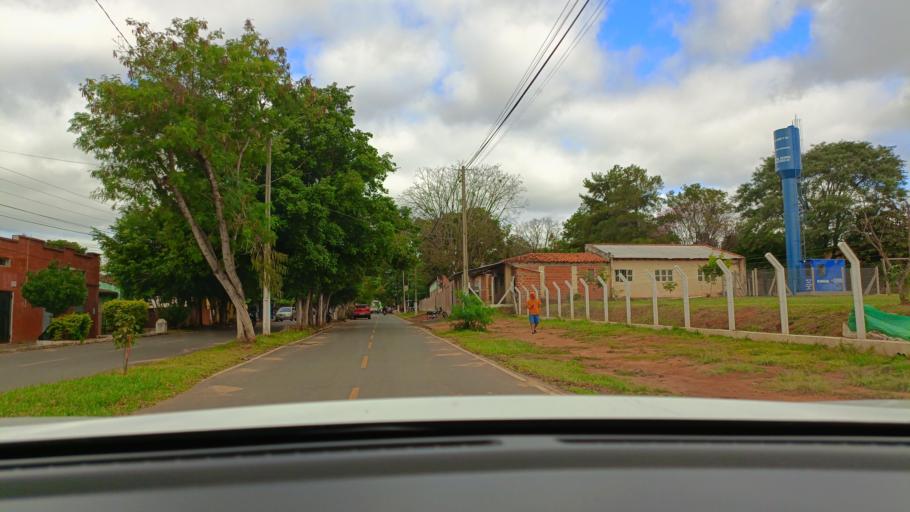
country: PY
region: San Pedro
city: Guayaybi
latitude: -24.6601
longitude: -56.4429
